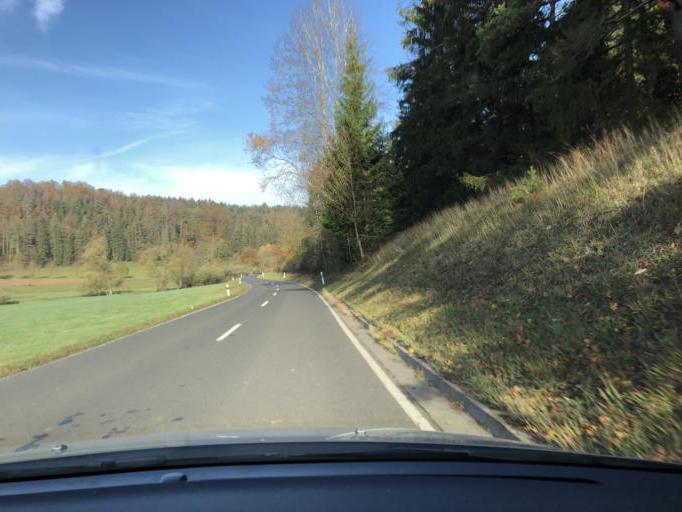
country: DE
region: Thuringia
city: Reurieth
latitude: 50.4444
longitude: 10.6473
